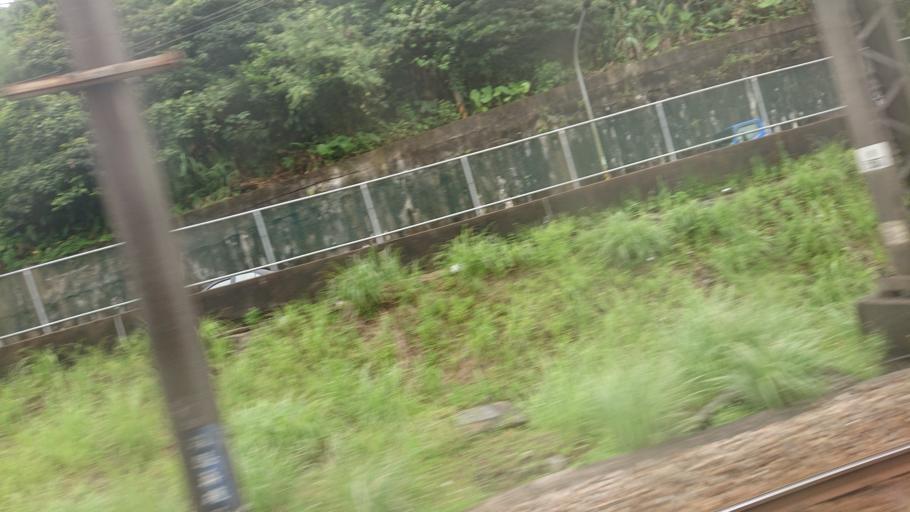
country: TW
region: Taiwan
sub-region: Keelung
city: Keelung
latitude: 25.0910
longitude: 121.7107
